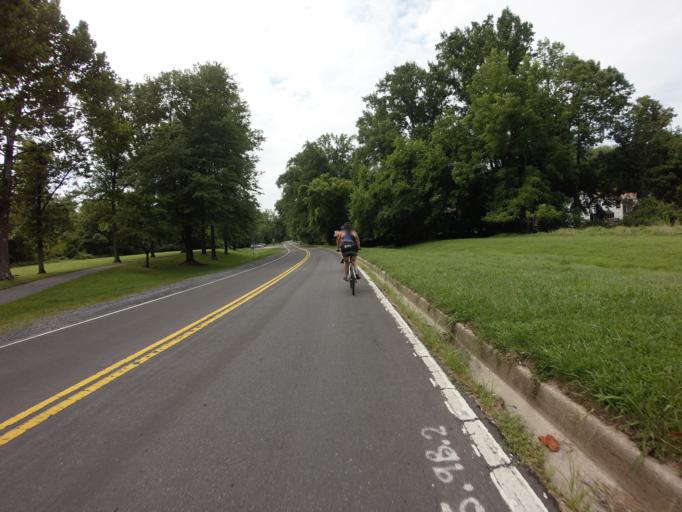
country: US
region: Maryland
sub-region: Montgomery County
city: Forest Glen
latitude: 39.0096
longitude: -77.0632
